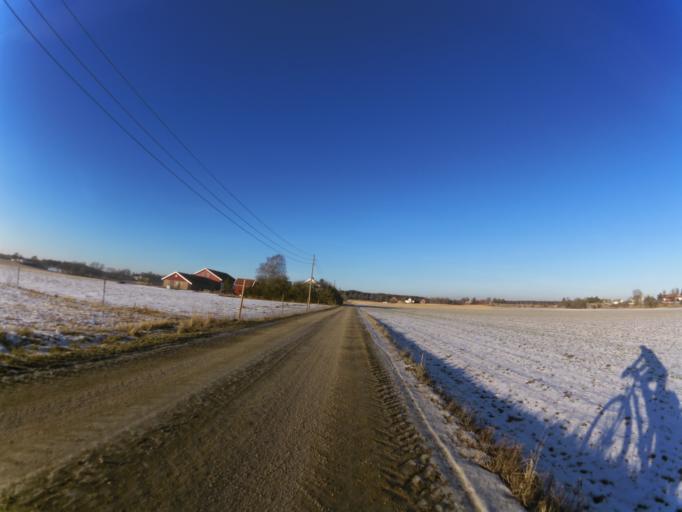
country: NO
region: Ostfold
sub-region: Fredrikstad
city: Lervik
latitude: 59.2471
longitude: 10.8112
